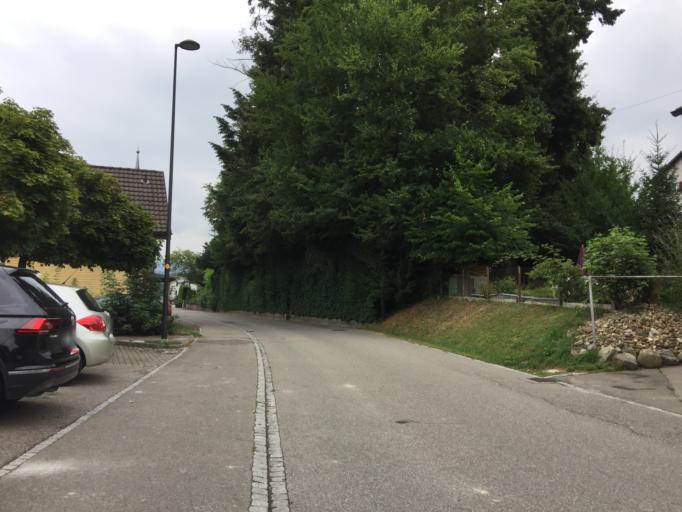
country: CH
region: Saint Gallen
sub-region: Wahlkreis Wil
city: Uzwil
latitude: 47.4338
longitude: 9.1358
